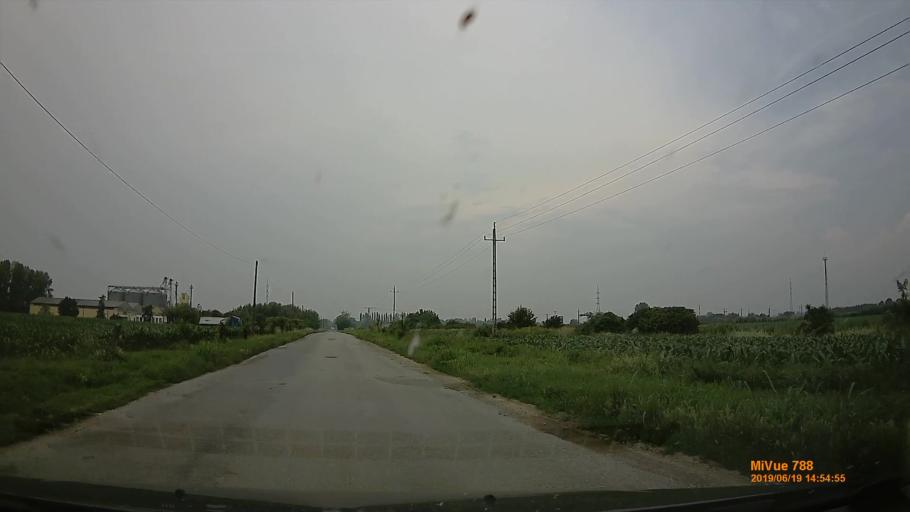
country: HU
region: Baranya
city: Szigetvar
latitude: 46.0374
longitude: 17.8210
